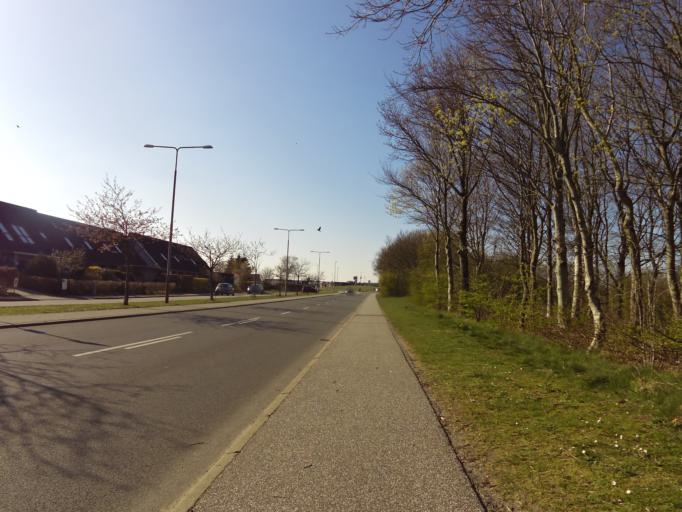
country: DK
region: South Denmark
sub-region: Esbjerg Kommune
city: Ribe
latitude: 55.3507
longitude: 8.7858
